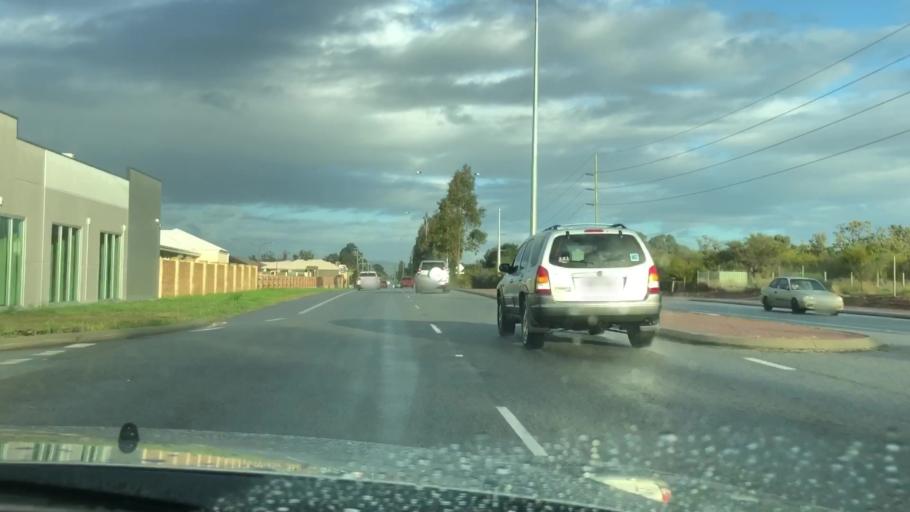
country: AU
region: Western Australia
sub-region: Armadale
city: Harrisdale
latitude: -32.1083
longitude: 115.9398
